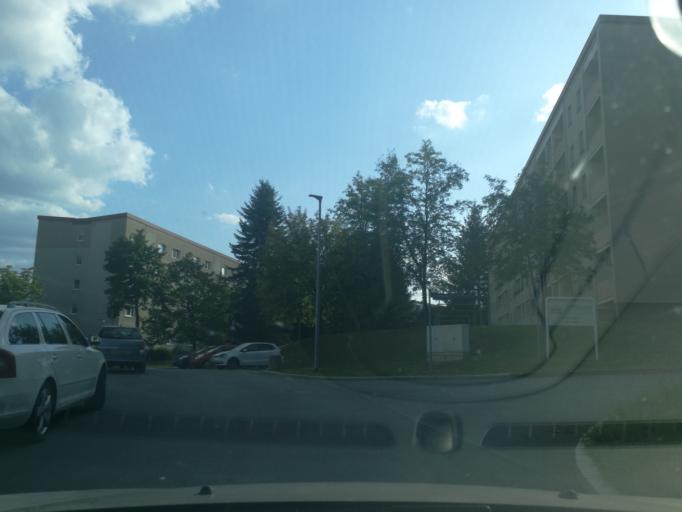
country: DE
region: Saxony
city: Adorf
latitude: 50.3154
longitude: 12.2493
